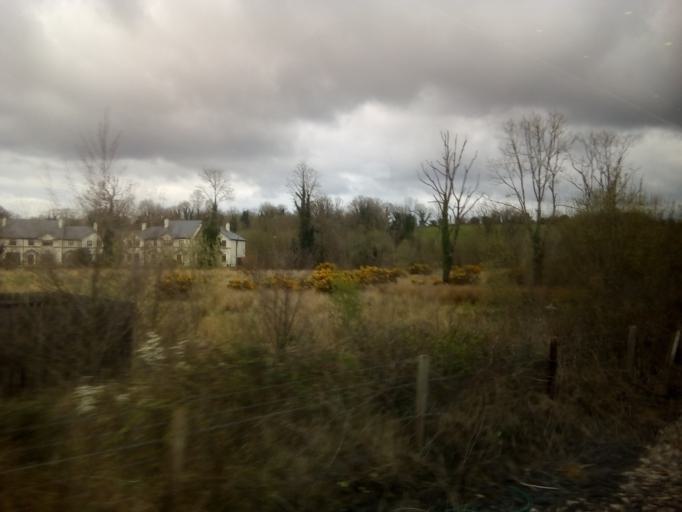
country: IE
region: Leinster
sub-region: An Longfort
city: Longford
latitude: 53.8572
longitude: -7.9149
